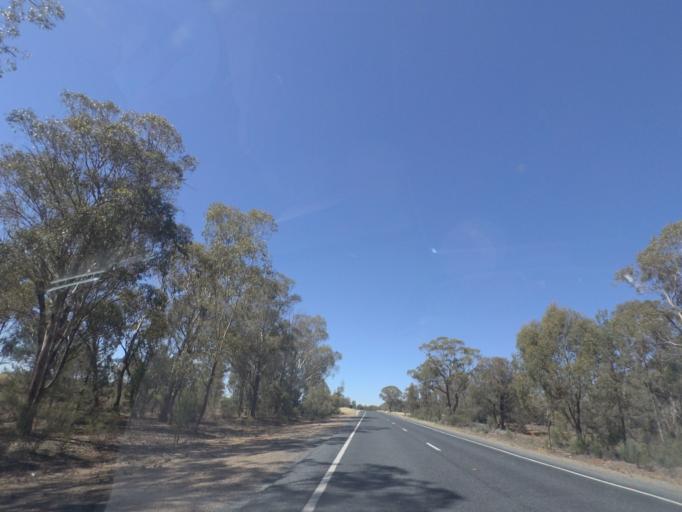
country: AU
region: New South Wales
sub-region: Narrandera
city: Narrandera
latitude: -34.4442
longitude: 146.8403
